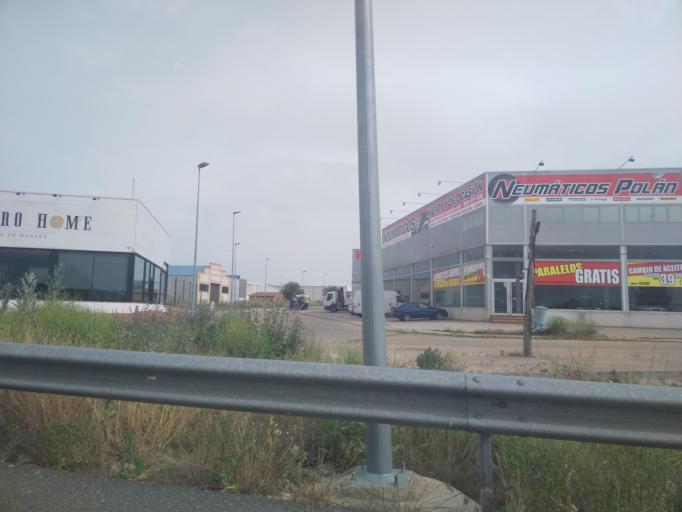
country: ES
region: Castille-La Mancha
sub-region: Province of Toledo
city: Guadamur
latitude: 39.8026
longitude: -4.1349
